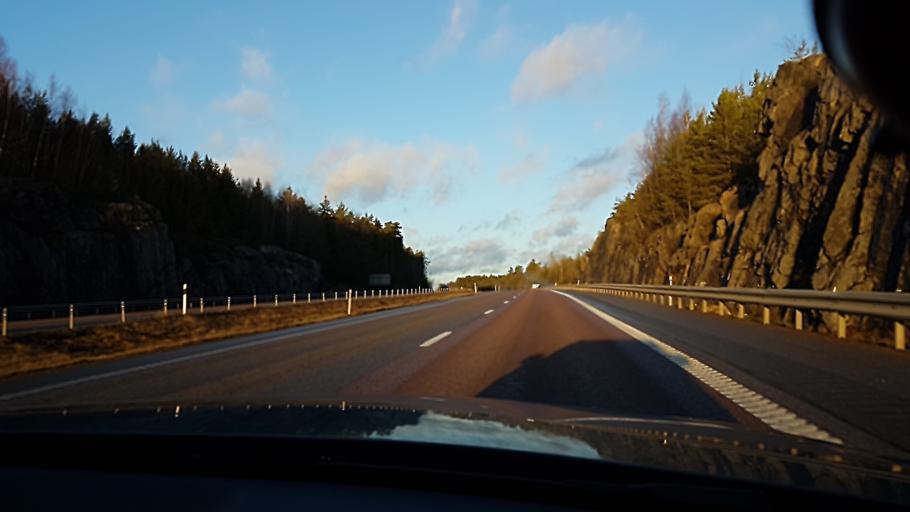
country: SE
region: Soedermanland
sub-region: Trosa Kommun
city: Vagnharad
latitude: 59.0185
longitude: 17.5514
